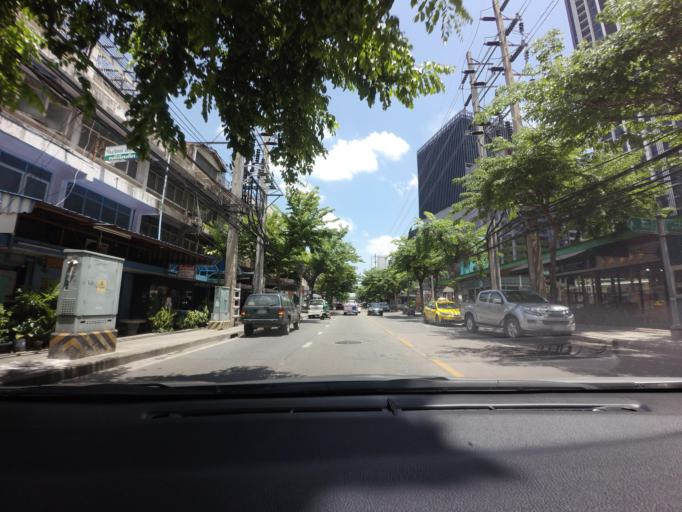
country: TH
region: Bangkok
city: Phra Khanong
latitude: 13.6844
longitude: 100.6125
